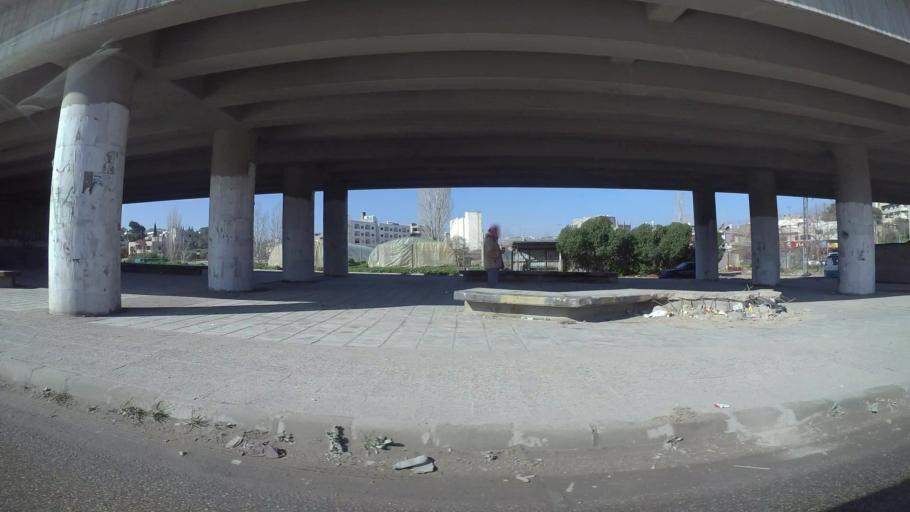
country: JO
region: Amman
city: Al Jubayhah
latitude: 32.0638
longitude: 35.8390
